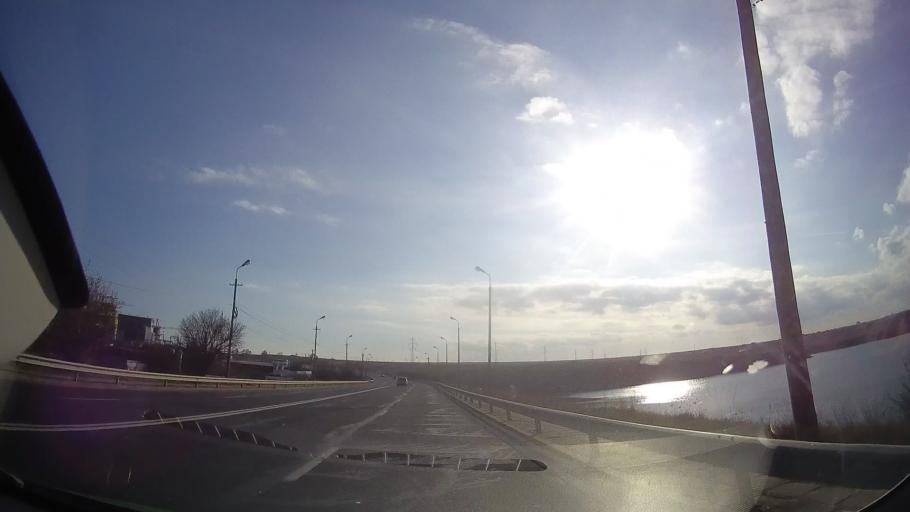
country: RO
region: Constanta
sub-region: Municipiul Mangalia
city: Mangalia
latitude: 43.8021
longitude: 28.5597
